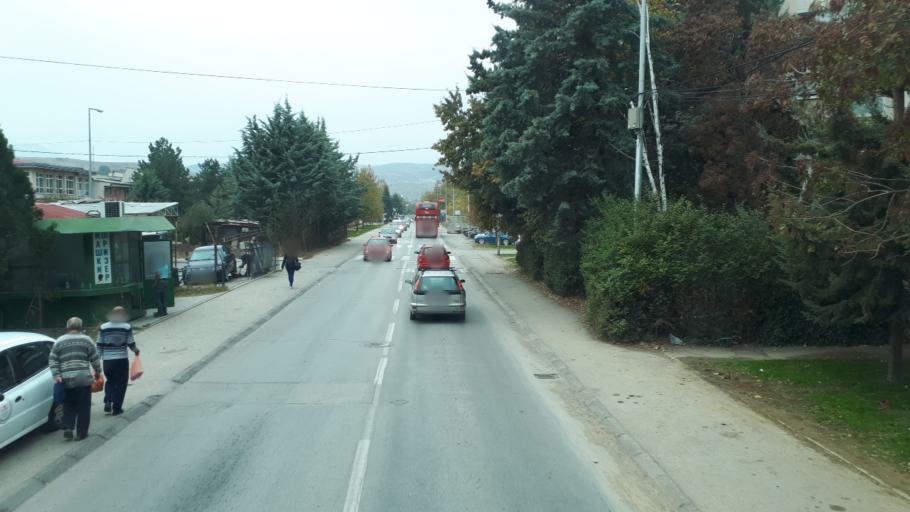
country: MK
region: Saraj
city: Saraj
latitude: 42.0174
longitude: 21.3562
